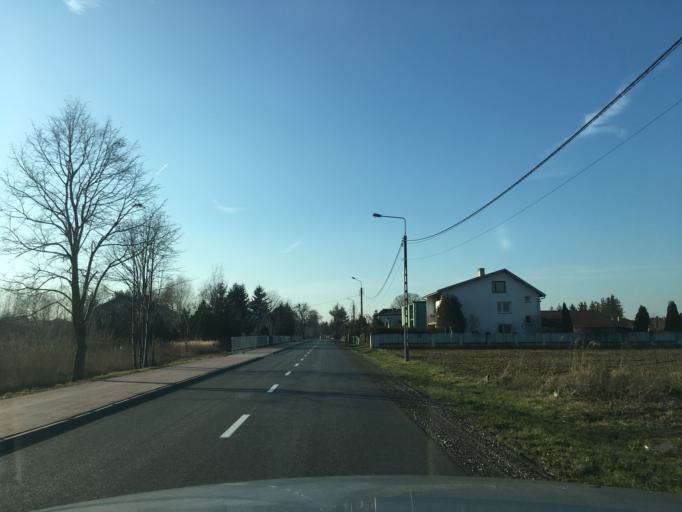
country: PL
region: Masovian Voivodeship
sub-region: Powiat pruszkowski
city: Nadarzyn
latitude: 52.0484
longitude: 20.7577
